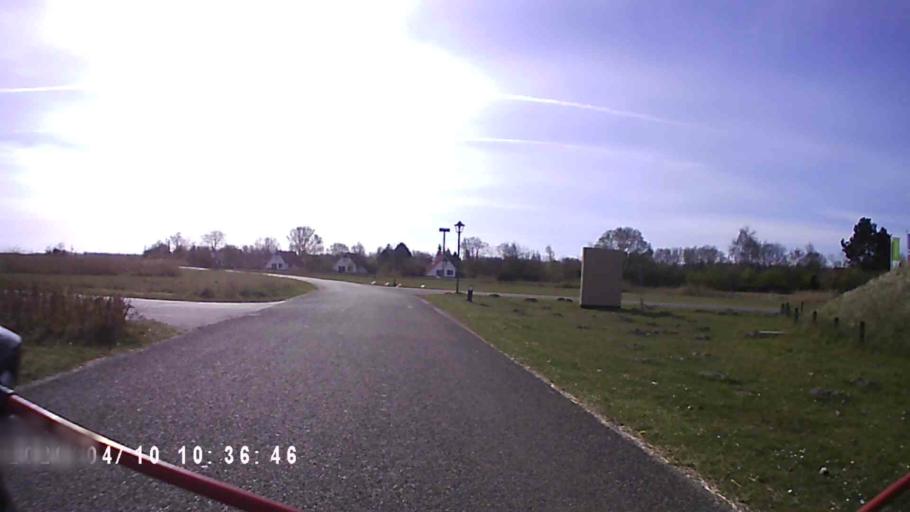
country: NL
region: Friesland
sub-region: Gemeente Dongeradeel
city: Anjum
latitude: 53.3901
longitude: 6.2160
